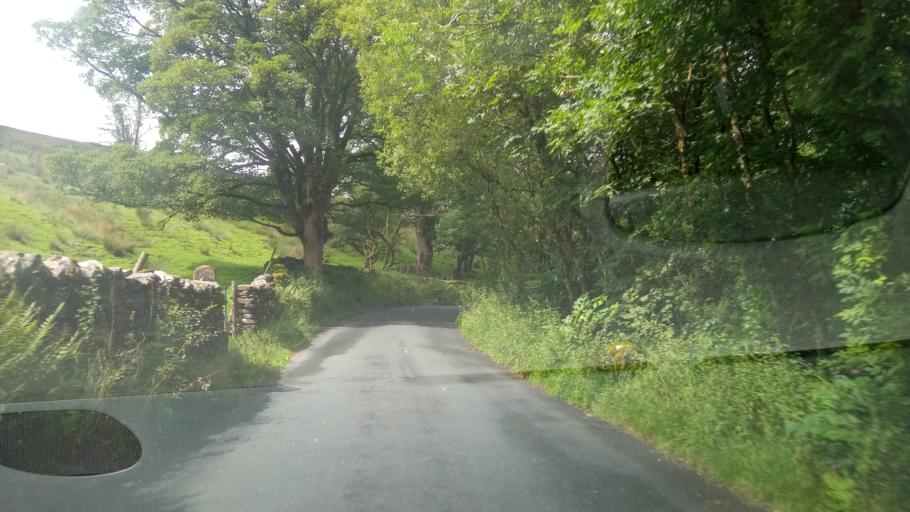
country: GB
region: England
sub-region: North Yorkshire
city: Ingleton
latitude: 54.2732
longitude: -2.3597
